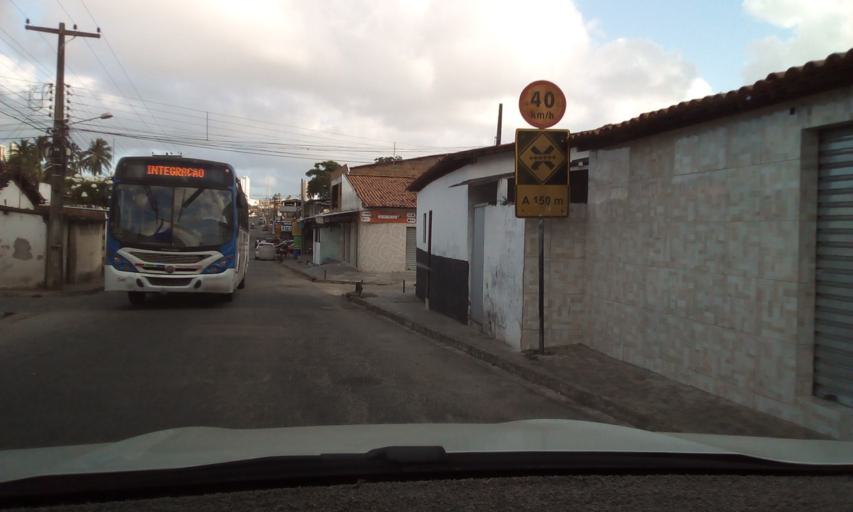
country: BR
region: Paraiba
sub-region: Joao Pessoa
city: Joao Pessoa
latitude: -7.0983
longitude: -34.8632
